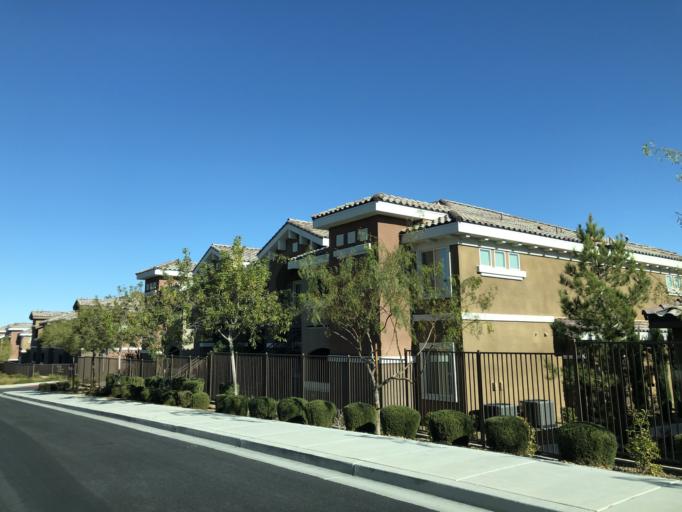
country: US
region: Nevada
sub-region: Clark County
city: Whitney
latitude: 36.0009
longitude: -115.0876
